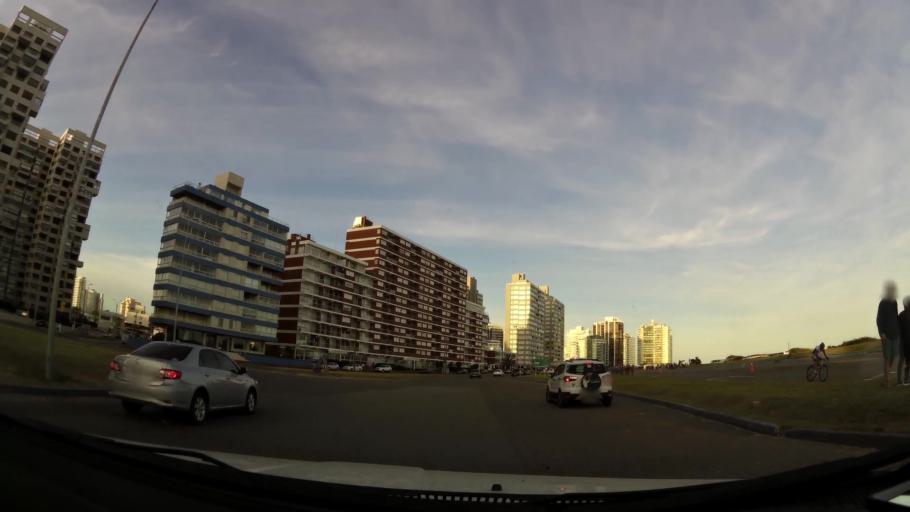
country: UY
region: Maldonado
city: Punta del Este
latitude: -34.9560
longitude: -54.9364
